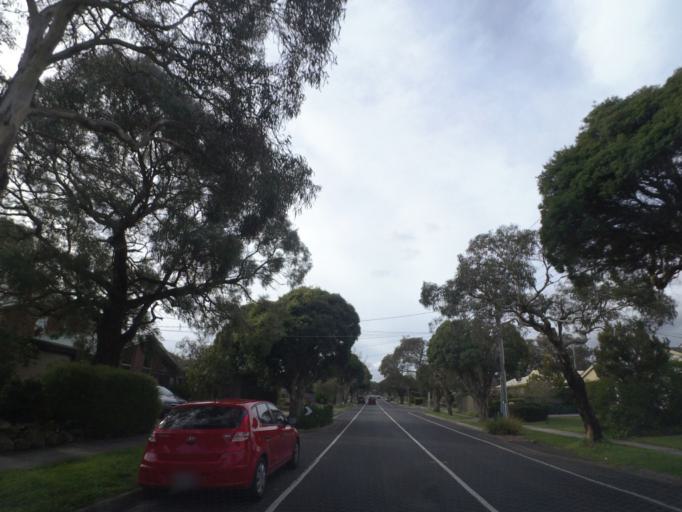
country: AU
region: Victoria
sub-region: Whitehorse
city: Vermont South
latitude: -37.8666
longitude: 145.1811
